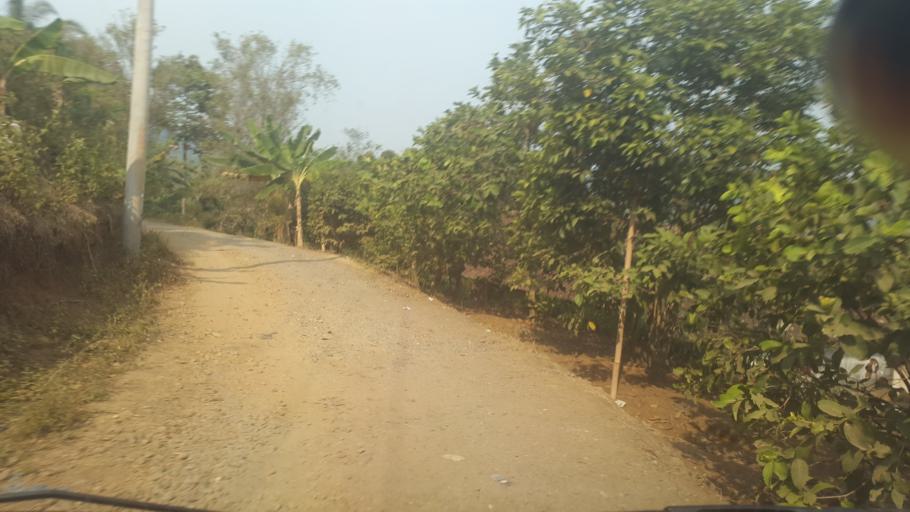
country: ID
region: West Java
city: Pelabuhanratu
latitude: -6.9433
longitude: 106.5472
